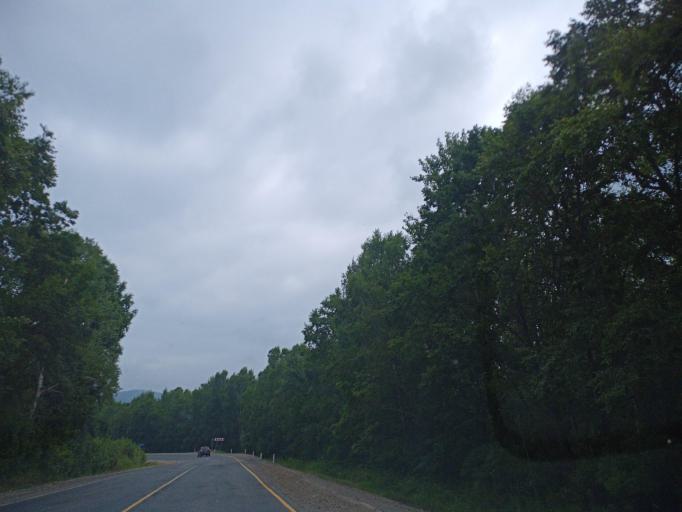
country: RU
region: Primorskiy
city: Dal'nerechensk
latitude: 46.0445
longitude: 133.8987
